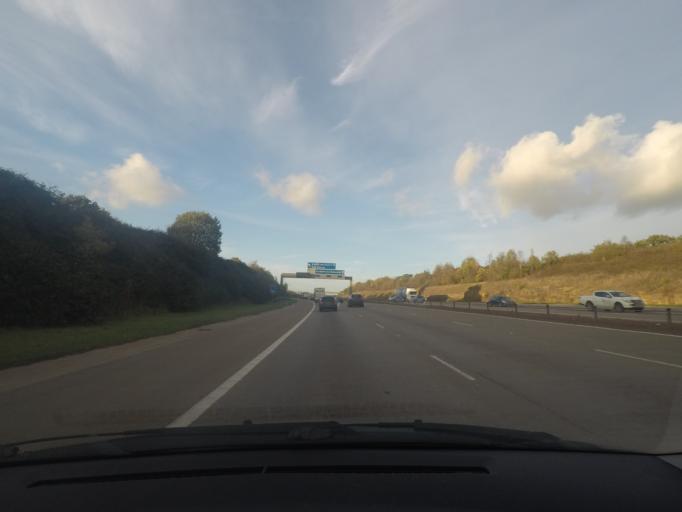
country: GB
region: England
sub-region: City and Borough of Leeds
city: Swillington
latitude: 53.7824
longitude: -1.4283
